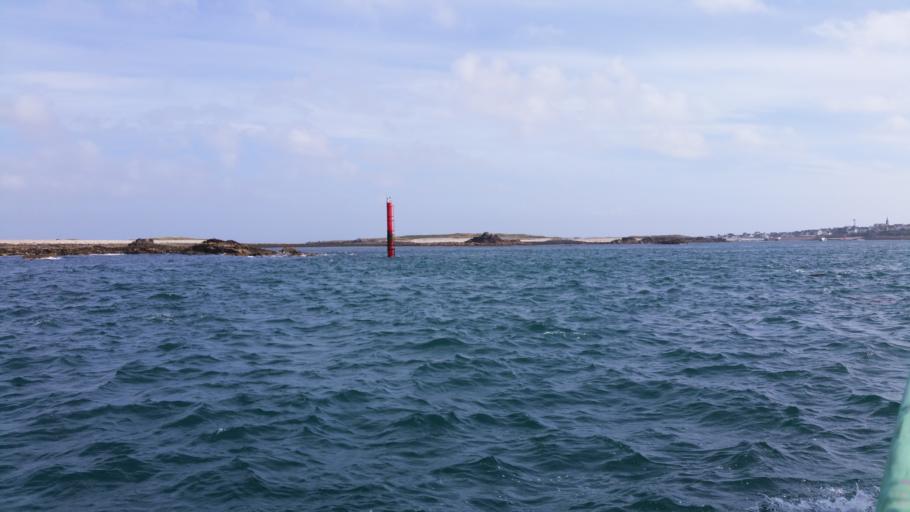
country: FR
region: Brittany
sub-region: Departement du Finistere
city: Le Conquet
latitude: 48.4102
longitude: -4.9510
